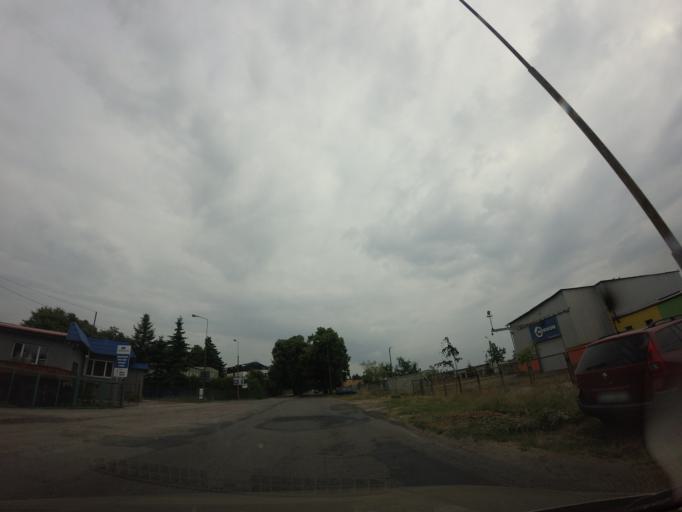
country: PL
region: West Pomeranian Voivodeship
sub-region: Powiat drawski
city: Czaplinek
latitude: 53.5494
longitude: 16.2323
